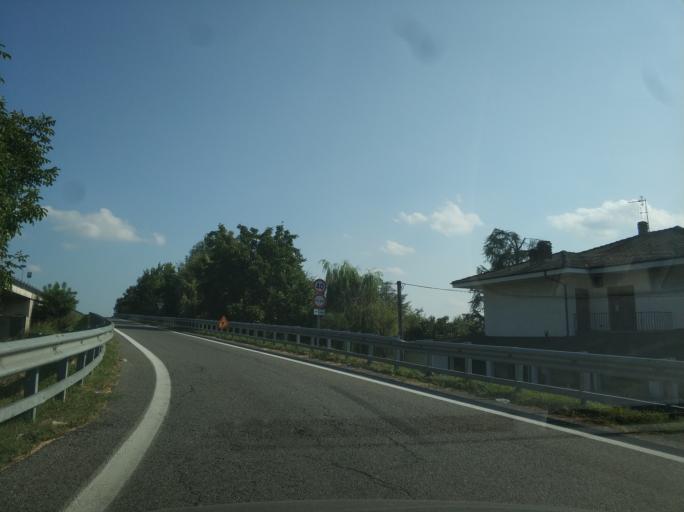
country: IT
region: Piedmont
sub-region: Provincia di Cuneo
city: Bandito
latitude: 44.6992
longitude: 7.8238
